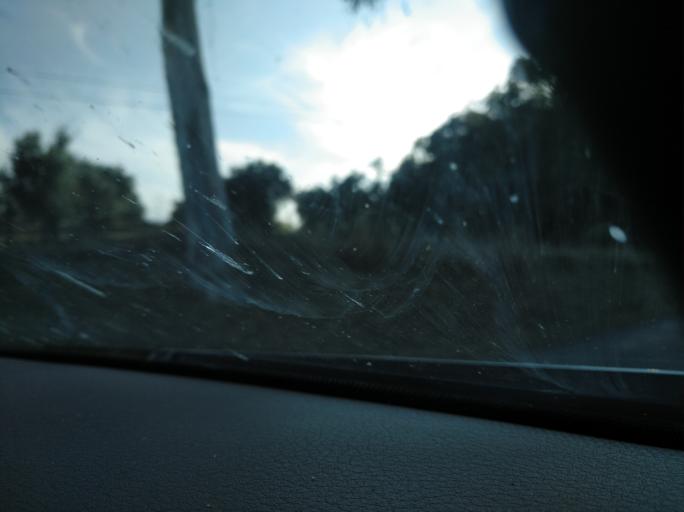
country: PT
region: Evora
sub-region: Borba
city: Borba
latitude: 38.9415
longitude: -7.4685
